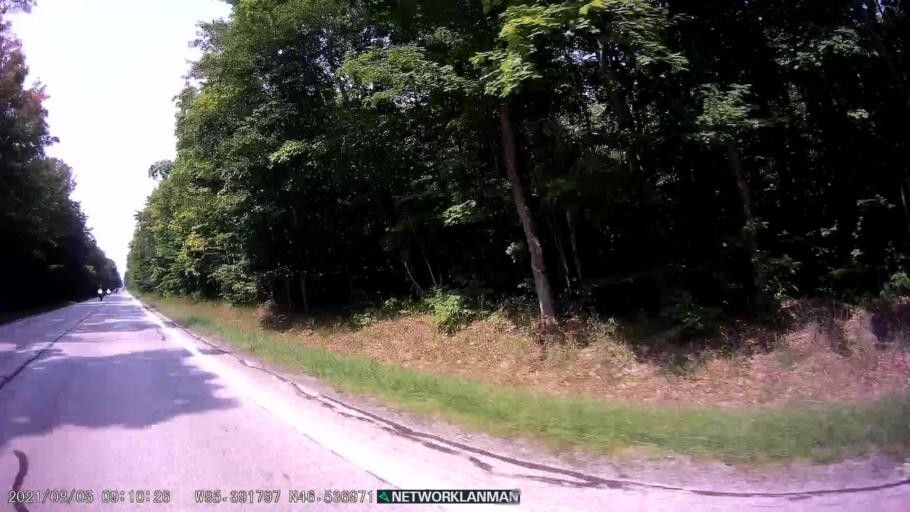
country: US
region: Michigan
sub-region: Luce County
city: Newberry
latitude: 46.5368
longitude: -85.3920
